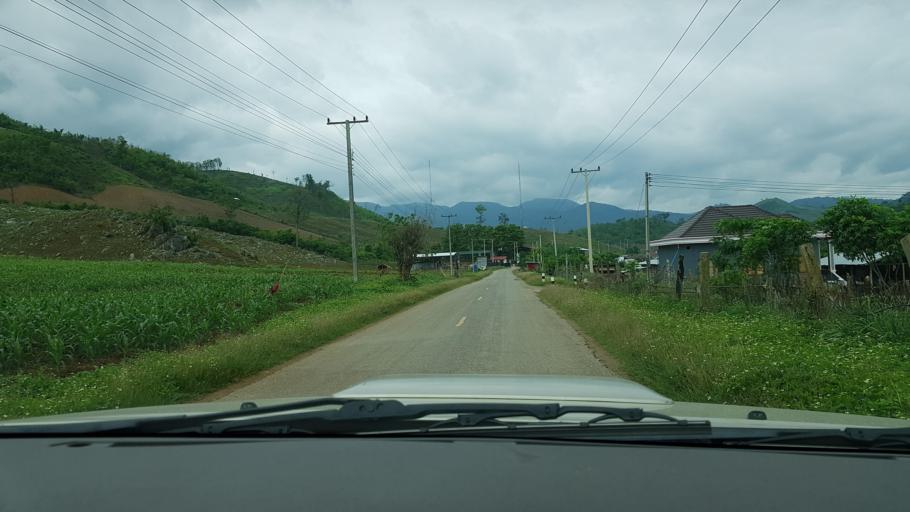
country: TH
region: Nan
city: Chaloem Phra Kiat
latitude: 19.9785
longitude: 101.2721
